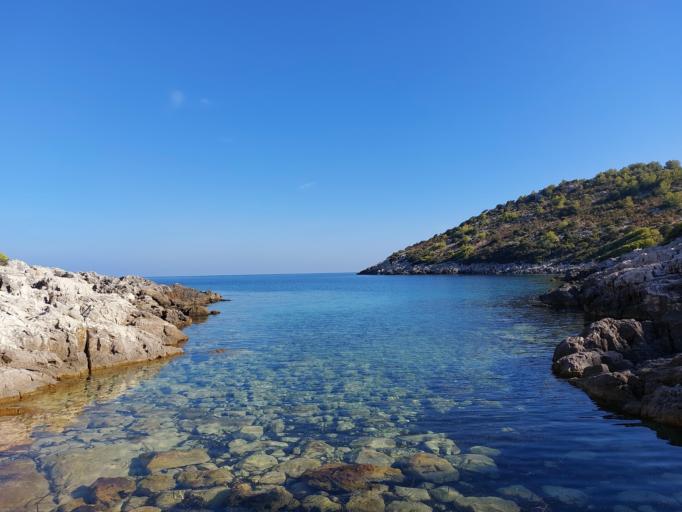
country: HR
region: Dubrovacko-Neretvanska
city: Smokvica
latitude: 42.7315
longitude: 16.8436
